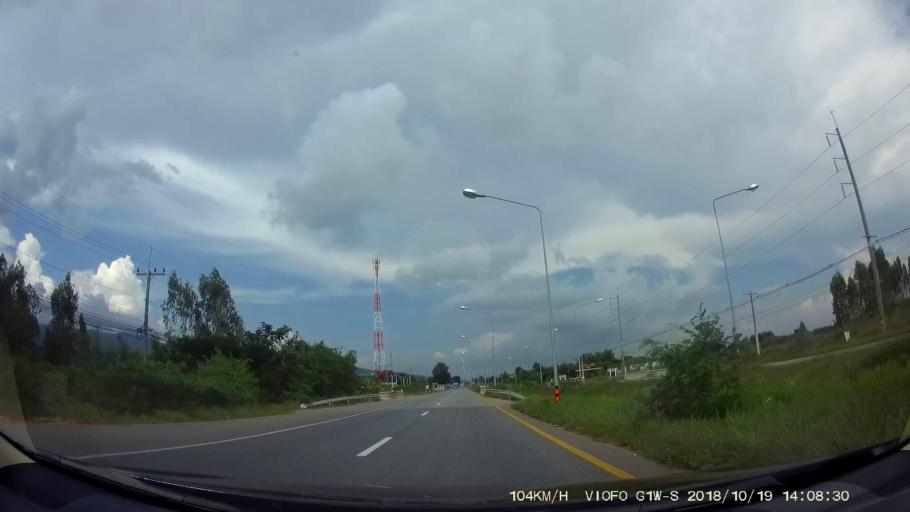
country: TH
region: Chaiyaphum
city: Chaiyaphum
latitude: 15.9074
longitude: 102.1248
